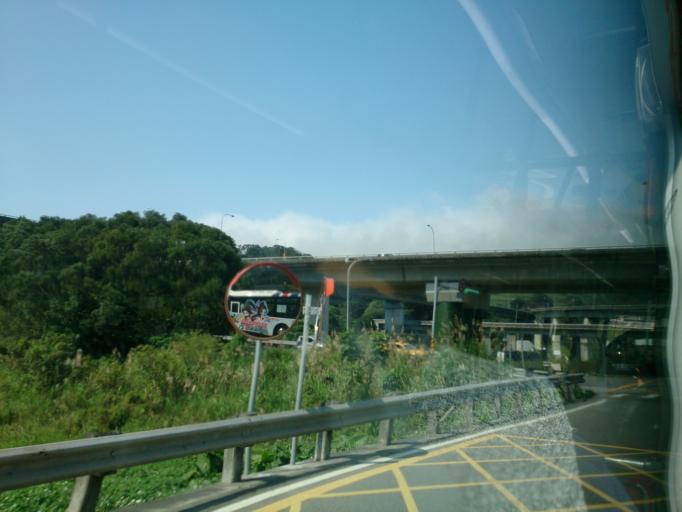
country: TW
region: Taipei
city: Taipei
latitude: 25.0009
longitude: 121.5962
